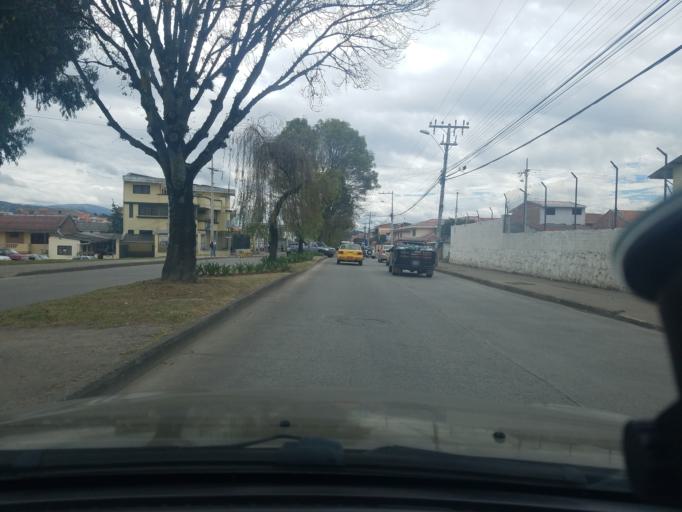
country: EC
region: Azuay
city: Cuenca
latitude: -2.9153
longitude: -79.0325
